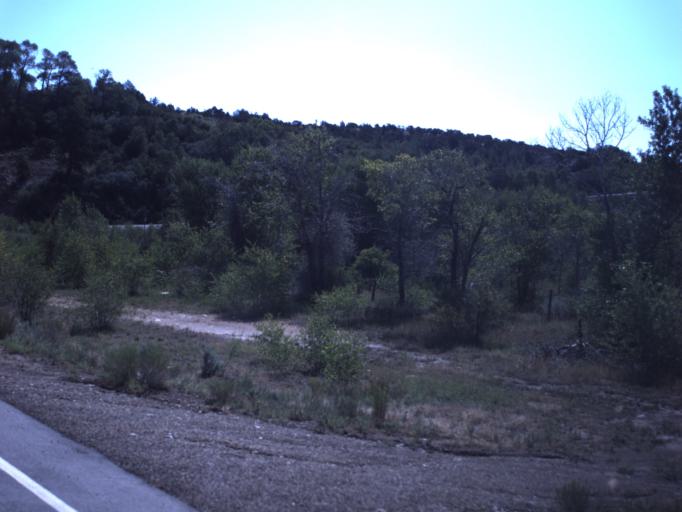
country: US
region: Utah
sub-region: Duchesne County
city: Duchesne
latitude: 40.3574
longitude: -110.3143
